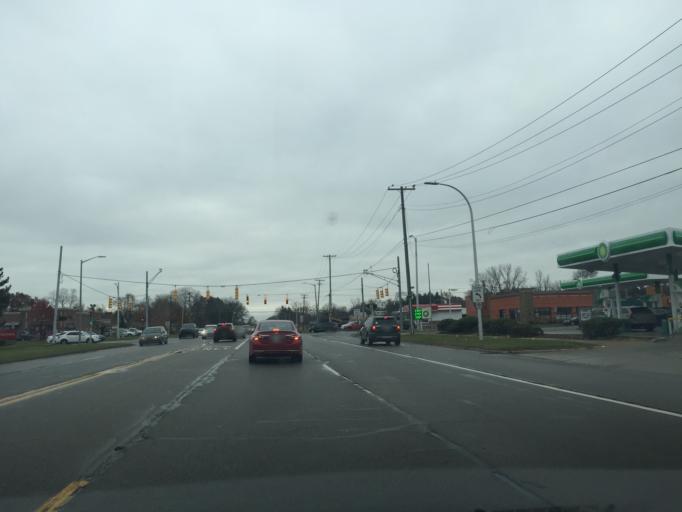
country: US
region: Michigan
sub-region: Wayne County
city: Livonia
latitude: 42.4135
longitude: -83.3353
